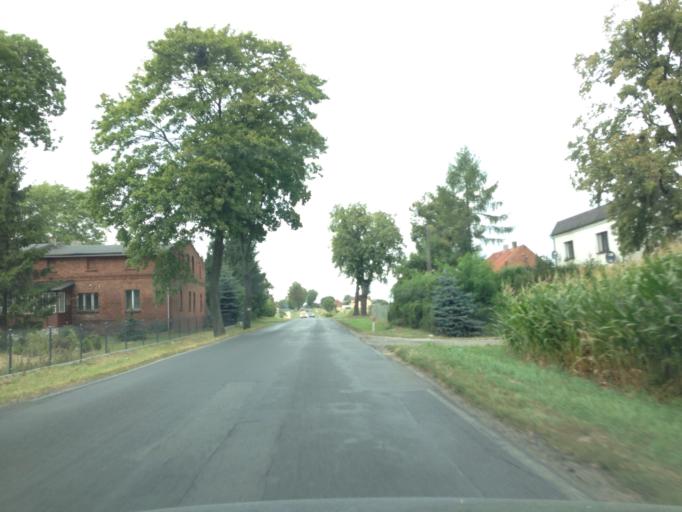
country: PL
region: Kujawsko-Pomorskie
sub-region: Powiat golubsko-dobrzynski
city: Golub-Dobrzyn
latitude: 53.1276
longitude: 19.0276
